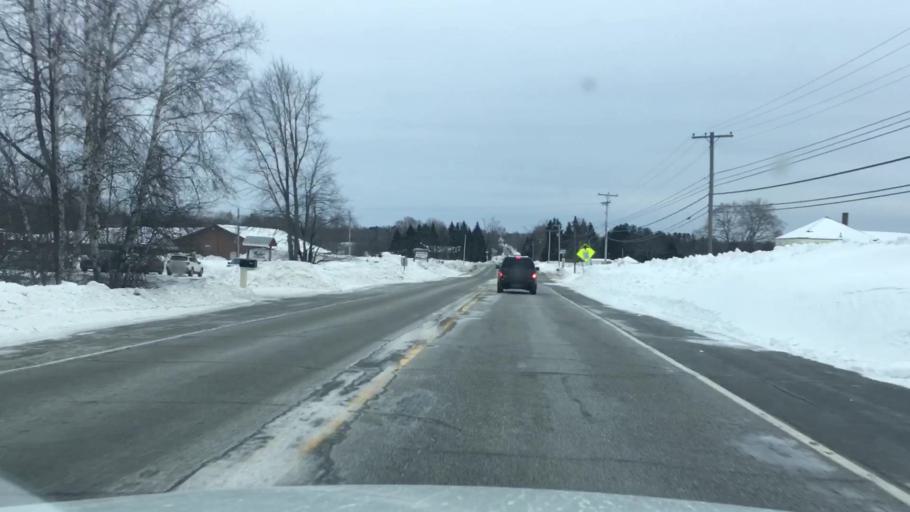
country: US
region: Maine
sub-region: Penobscot County
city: Charleston
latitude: 45.0190
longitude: -69.0285
